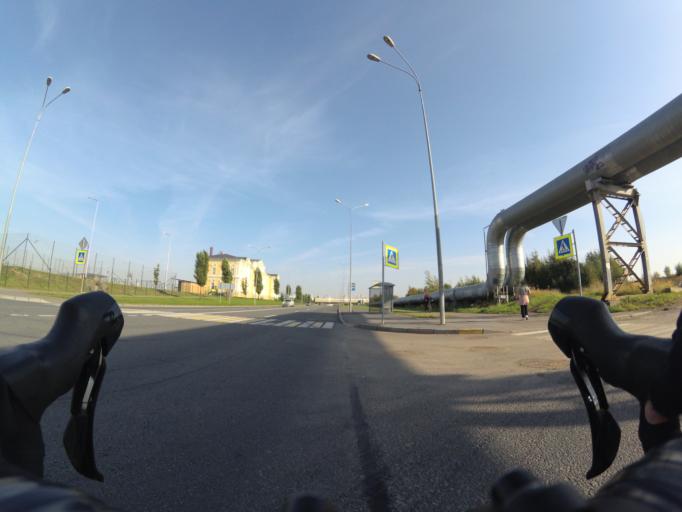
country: RU
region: St.-Petersburg
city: Staraya Derevnya
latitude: 59.9932
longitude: 30.2244
